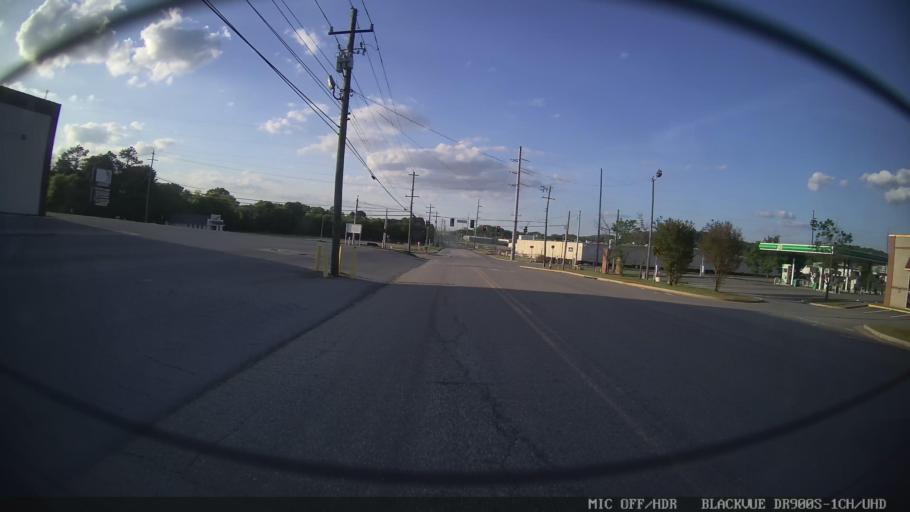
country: US
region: Georgia
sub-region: Bartow County
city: Cartersville
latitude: 34.1505
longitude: -84.7936
